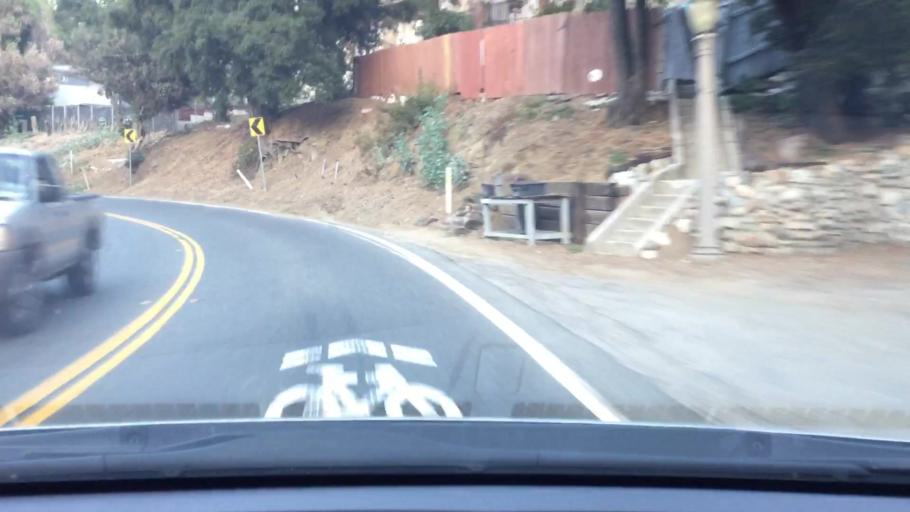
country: US
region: California
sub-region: San Bernardino County
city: Chino Hills
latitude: 33.9467
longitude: -117.7802
